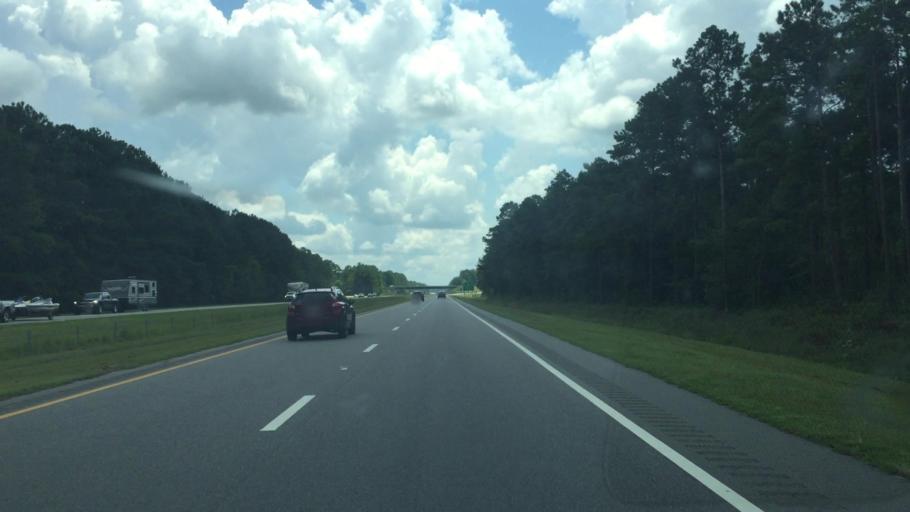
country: US
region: North Carolina
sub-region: Columbus County
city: Chadbourn
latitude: 34.3665
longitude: -78.8369
